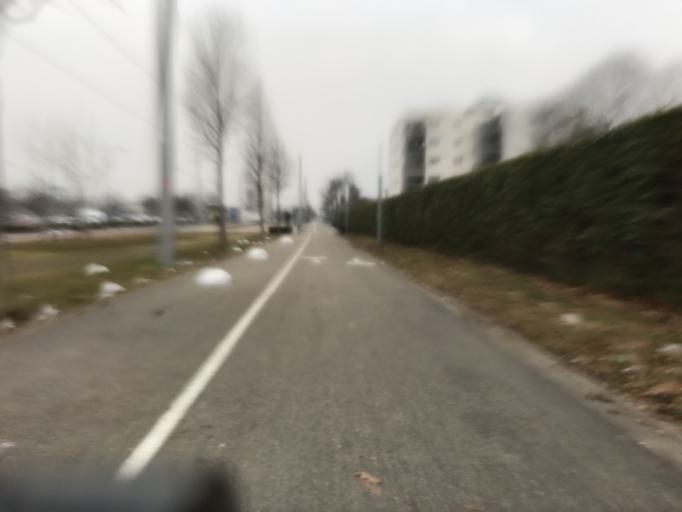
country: FR
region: Rhone-Alpes
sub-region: Departement de l'Isere
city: Seyssinet-Pariset
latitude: 45.1757
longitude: 5.6942
